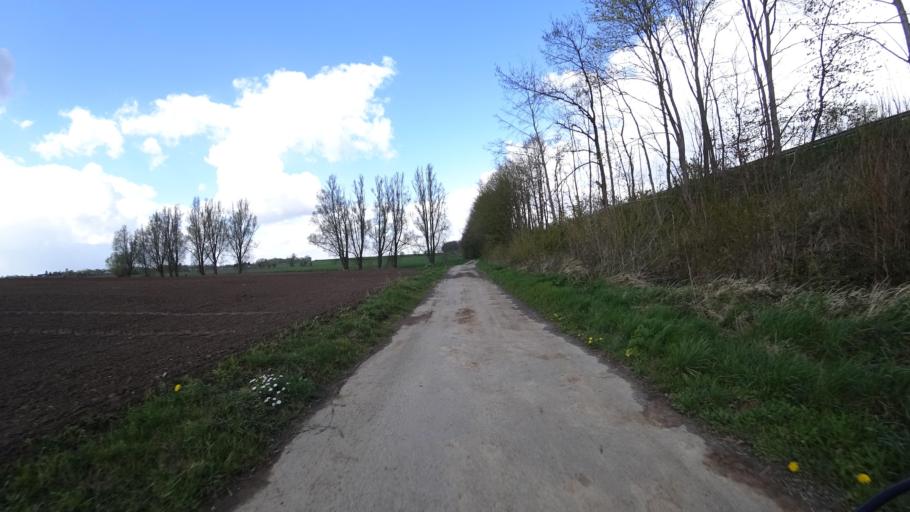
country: BE
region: Wallonia
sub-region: Province du Brabant Wallon
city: Walhain-Saint-Paul
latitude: 50.6501
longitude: 4.7037
